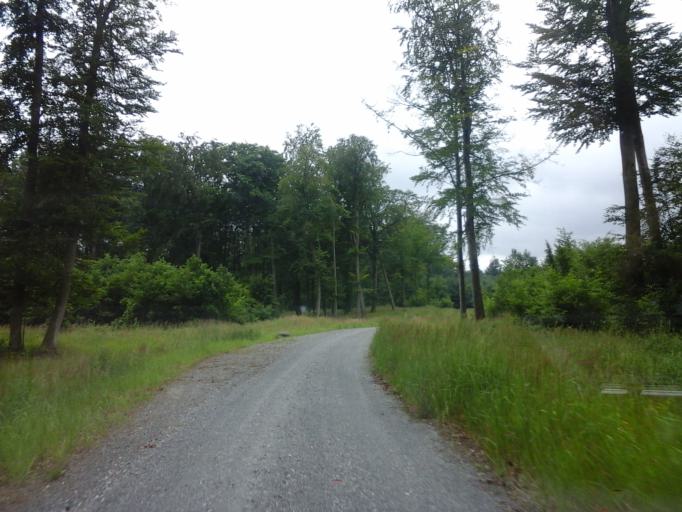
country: PL
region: West Pomeranian Voivodeship
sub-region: Powiat choszczenski
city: Krzecin
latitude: 52.9994
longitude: 15.4779
